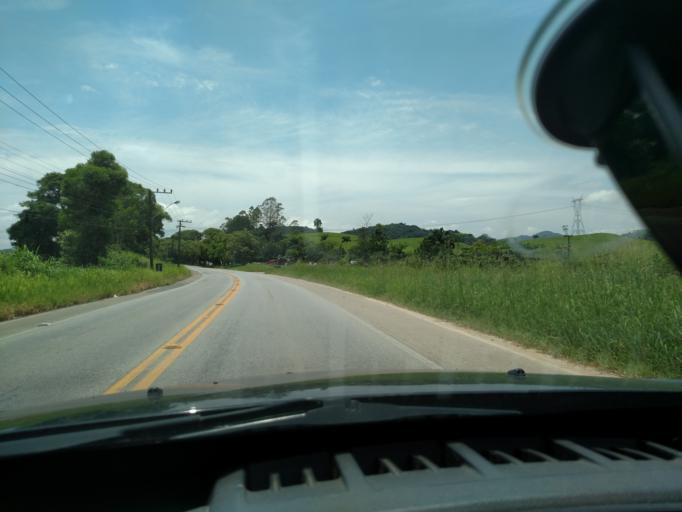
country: BR
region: Santa Catarina
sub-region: Gaspar
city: Gaspar
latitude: -26.9271
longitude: -48.8884
